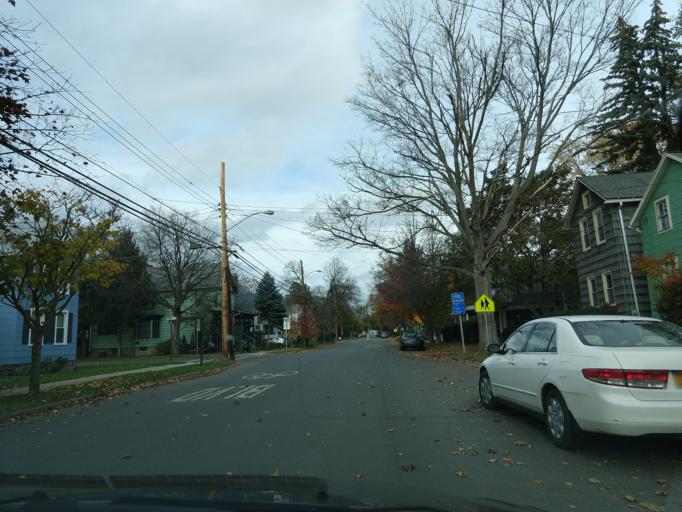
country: US
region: New York
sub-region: Tompkins County
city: Ithaca
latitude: 42.4493
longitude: -76.4974
